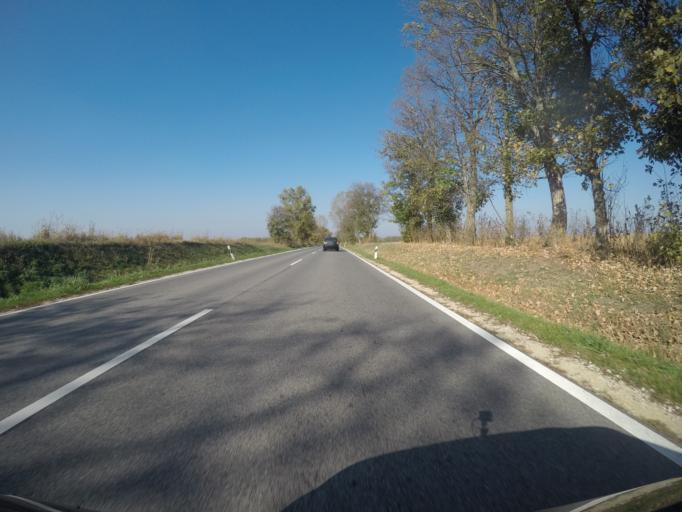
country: HU
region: Tolna
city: Tengelic
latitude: 46.5524
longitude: 18.6515
